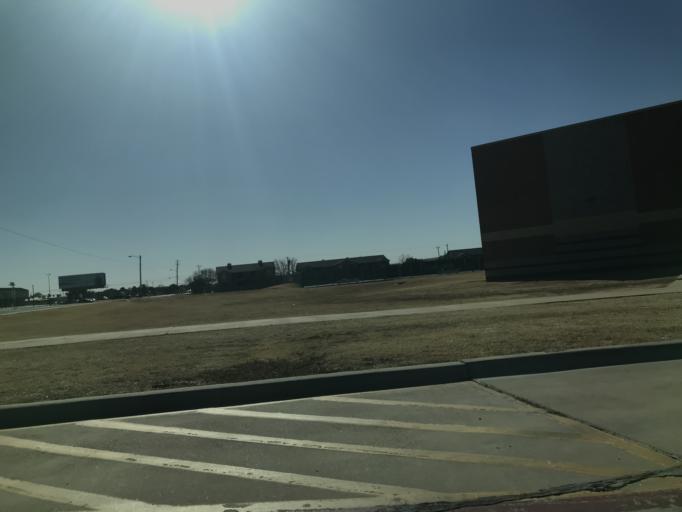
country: US
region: Texas
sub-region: Taylor County
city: Abilene
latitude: 32.4416
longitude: -99.7062
